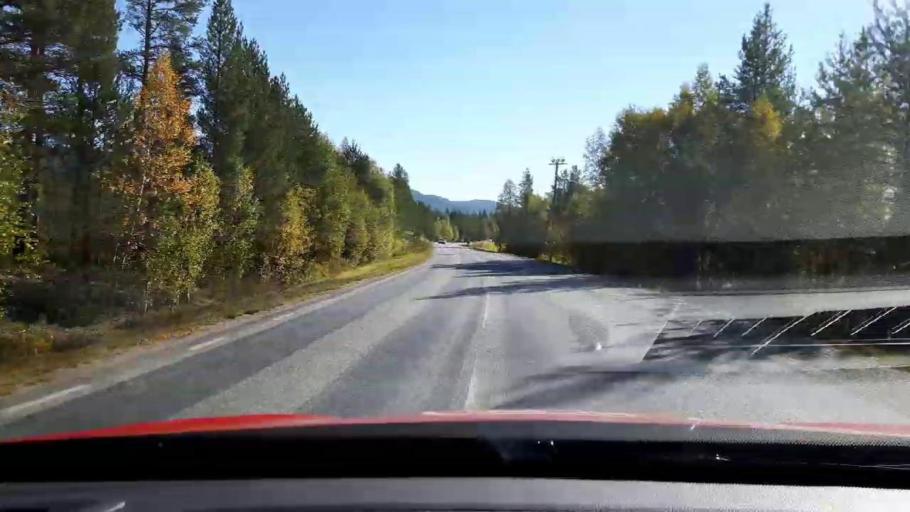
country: SE
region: Jaemtland
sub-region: Harjedalens Kommun
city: Sveg
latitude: 62.3637
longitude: 13.9976
